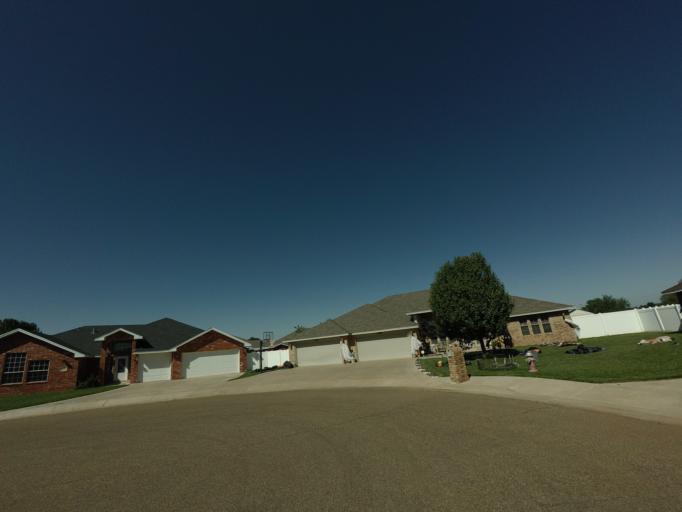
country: US
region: New Mexico
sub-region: Curry County
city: Clovis
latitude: 34.4316
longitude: -103.1710
